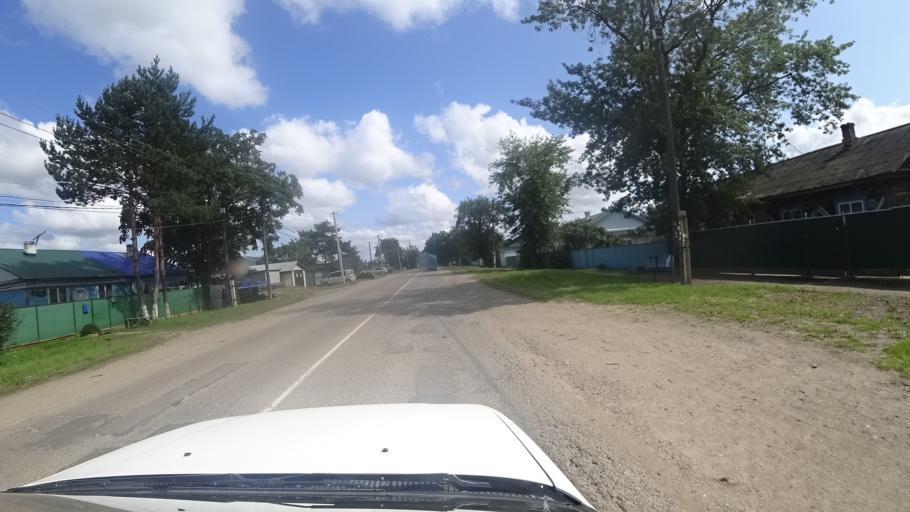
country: RU
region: Primorskiy
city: Dal'nerechensk
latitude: 45.9287
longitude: 133.7642
